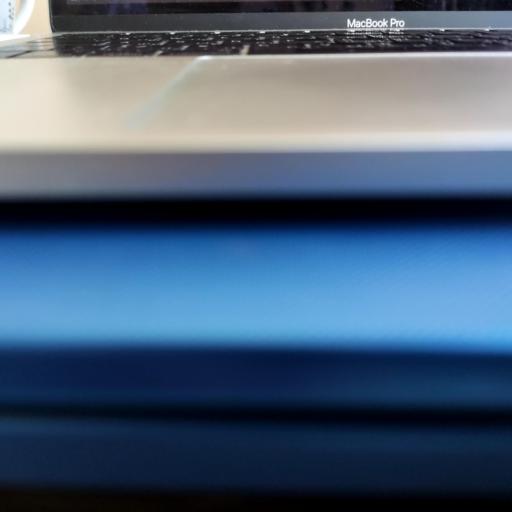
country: RU
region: Moscow
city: Khimki
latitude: 55.9116
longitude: 37.4546
